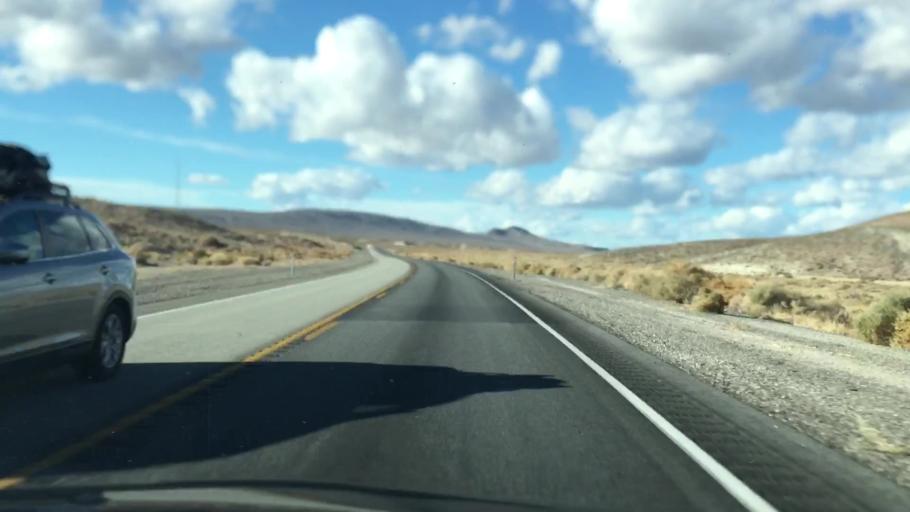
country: US
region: Nevada
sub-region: Nye County
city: Beatty
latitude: 37.0350
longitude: -116.7603
